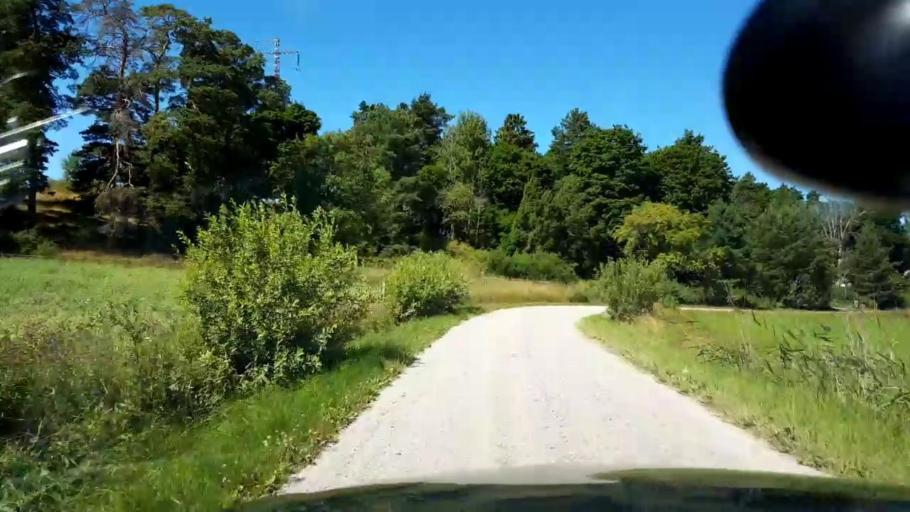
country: SE
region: Stockholm
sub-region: Upplands-Bro Kommun
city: Bro
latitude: 59.6149
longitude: 17.6157
